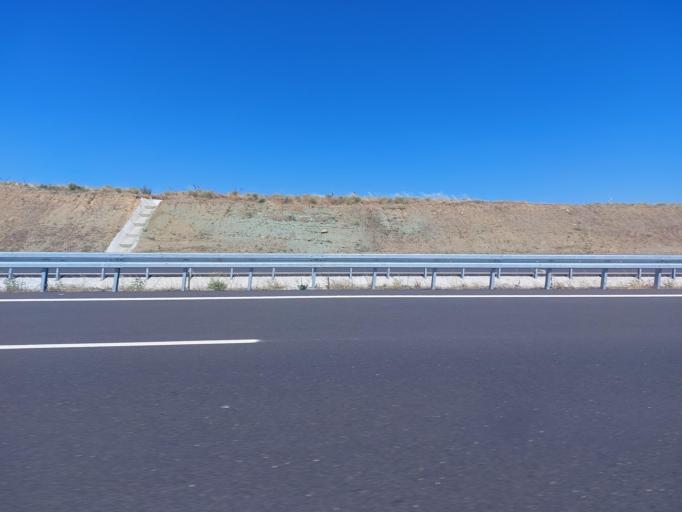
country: TR
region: Tekirdag
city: Balli
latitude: 40.7370
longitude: 26.9888
